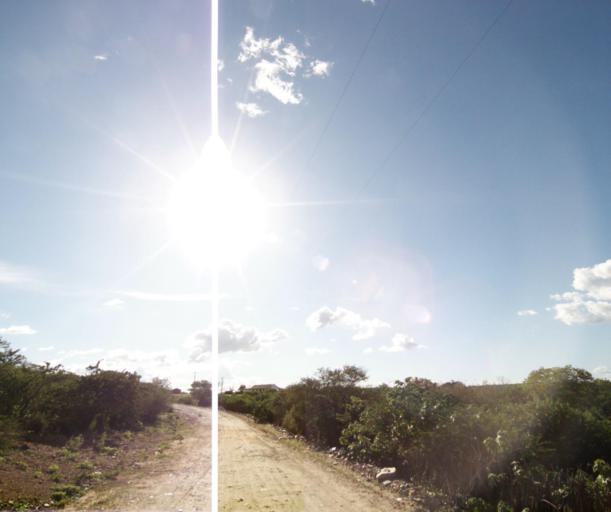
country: BR
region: Bahia
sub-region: Tanhacu
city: Tanhacu
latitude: -14.1825
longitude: -41.0110
